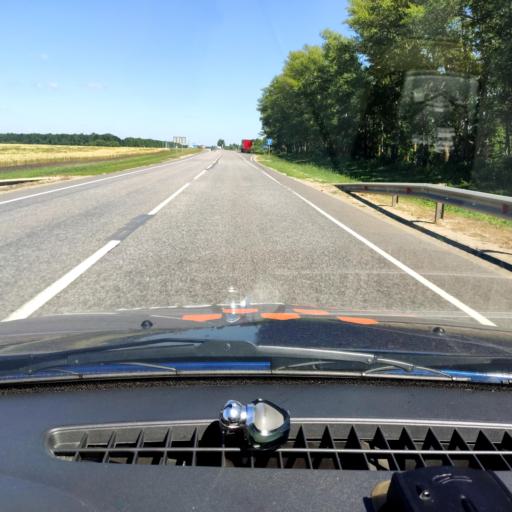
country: RU
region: Orjol
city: Pokrovskoye
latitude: 52.6204
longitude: 36.7621
